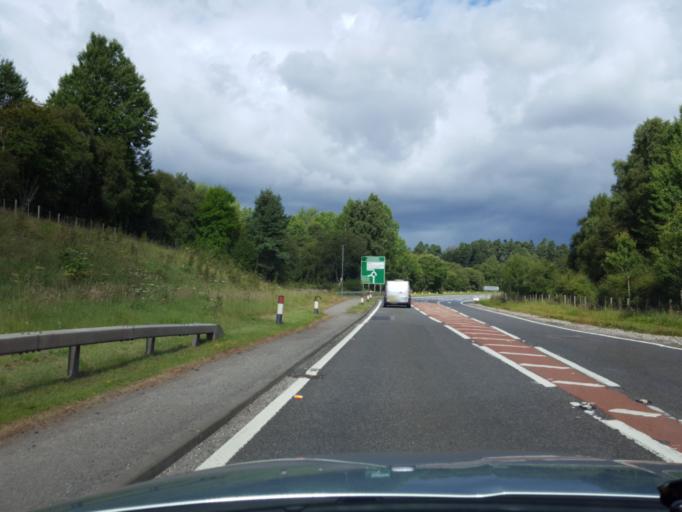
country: GB
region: Scotland
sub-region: Highland
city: Grantown on Spey
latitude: 57.3185
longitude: -3.6040
